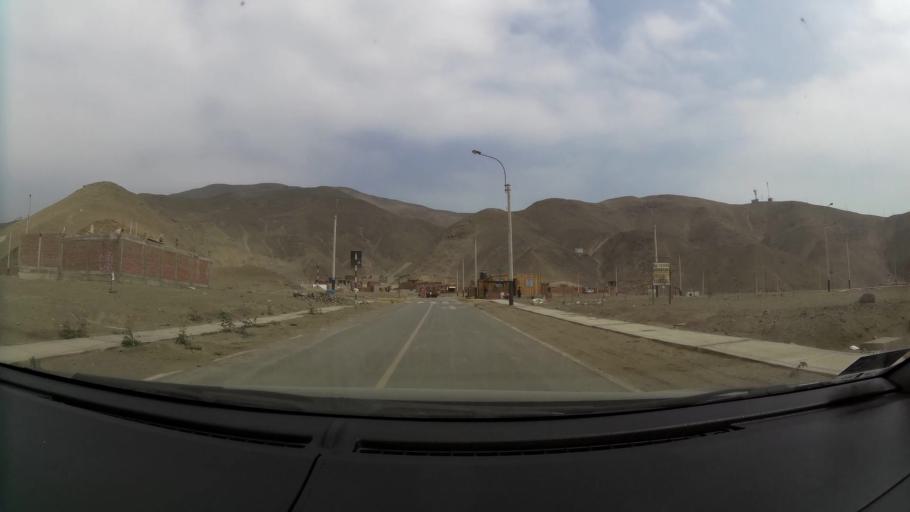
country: PE
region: Lima
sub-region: Lima
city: Santa Rosa
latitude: -11.7947
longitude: -77.1494
